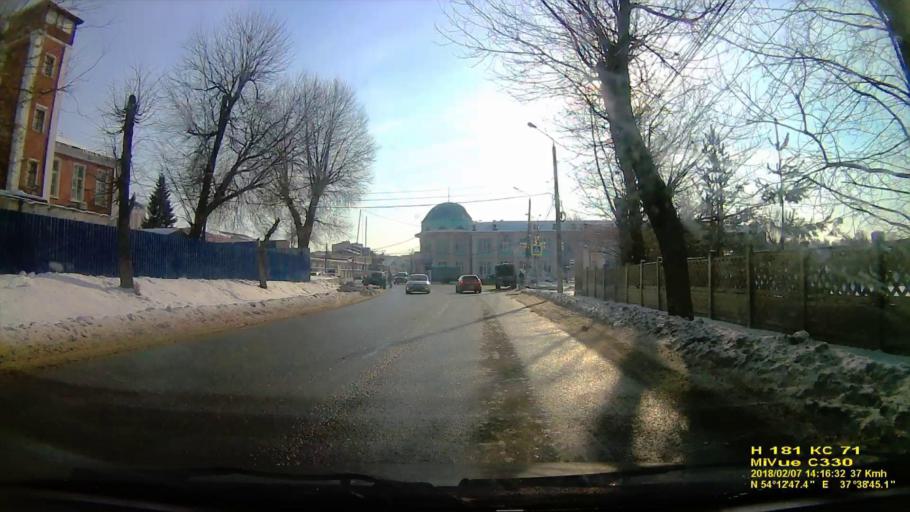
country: RU
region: Tula
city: Tula
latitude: 54.2133
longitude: 37.6459
